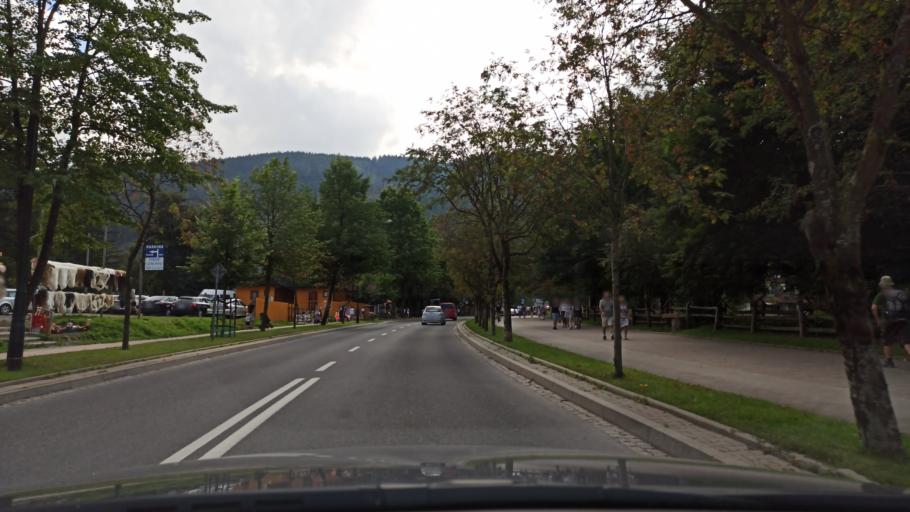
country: PL
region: Lesser Poland Voivodeship
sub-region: Powiat tatrzanski
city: Zakopane
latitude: 49.2839
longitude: 19.9645
